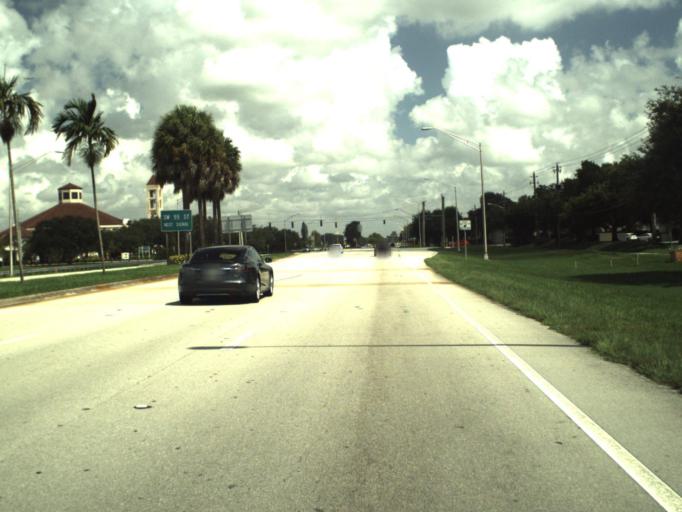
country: US
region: Florida
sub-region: Broward County
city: Sunshine Ranches
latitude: 26.0468
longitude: -80.3129
